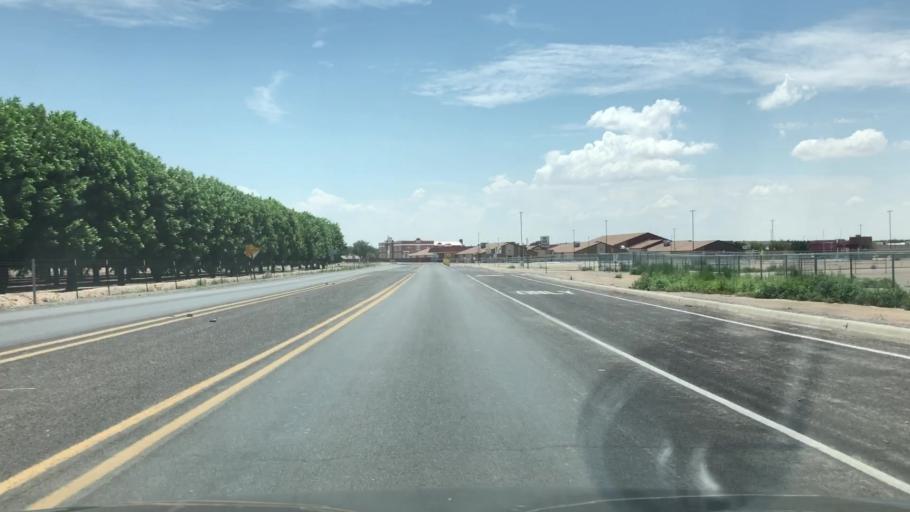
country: US
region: New Mexico
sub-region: Dona Ana County
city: La Union
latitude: 32.0011
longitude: -106.6567
